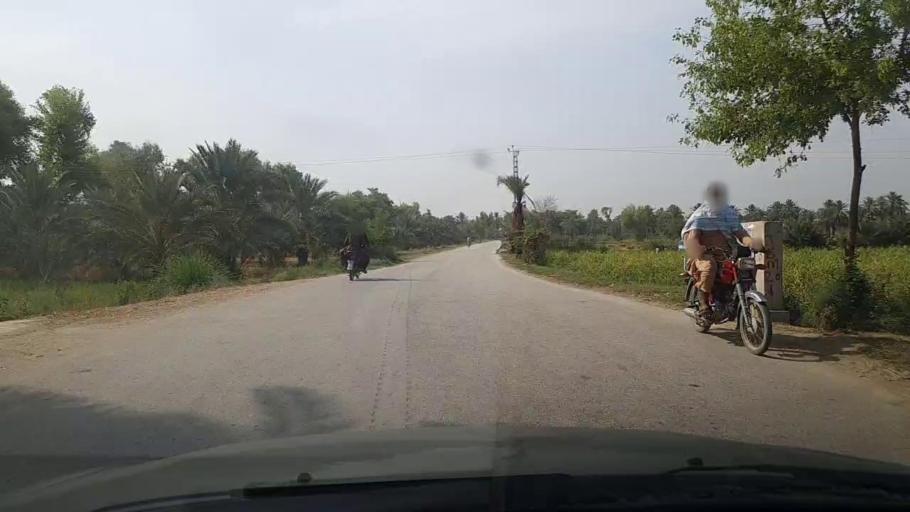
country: PK
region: Sindh
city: Gambat
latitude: 27.4546
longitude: 68.4860
